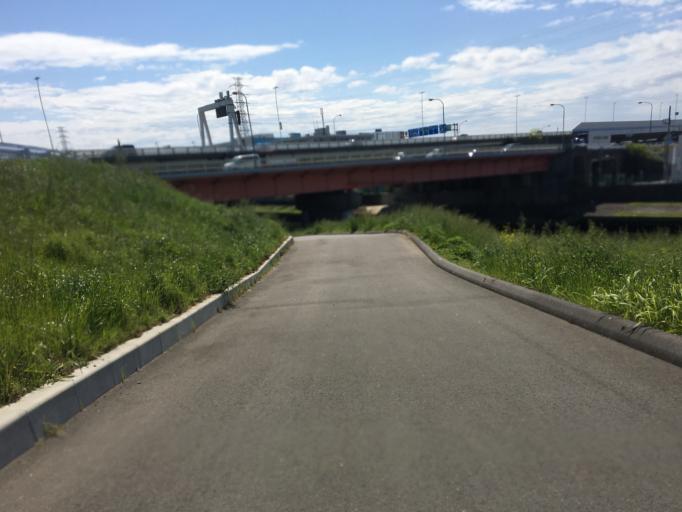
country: JP
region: Saitama
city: Wako
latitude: 35.7974
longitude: 139.6450
